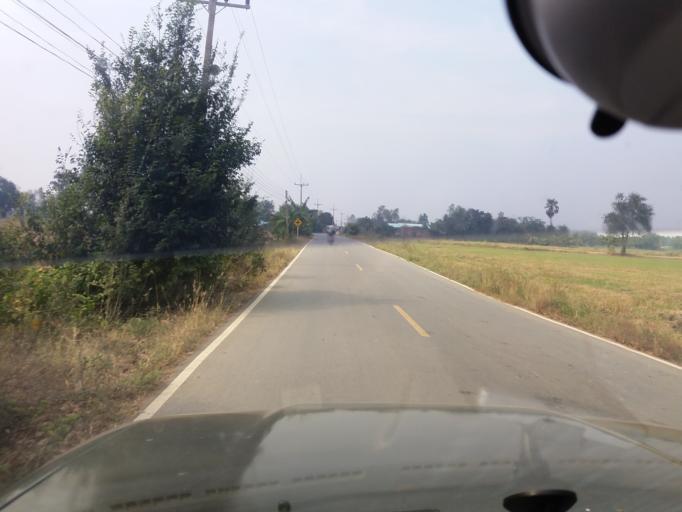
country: TH
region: Suphan Buri
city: Doem Bang Nang Buat
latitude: 14.8921
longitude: 100.1674
